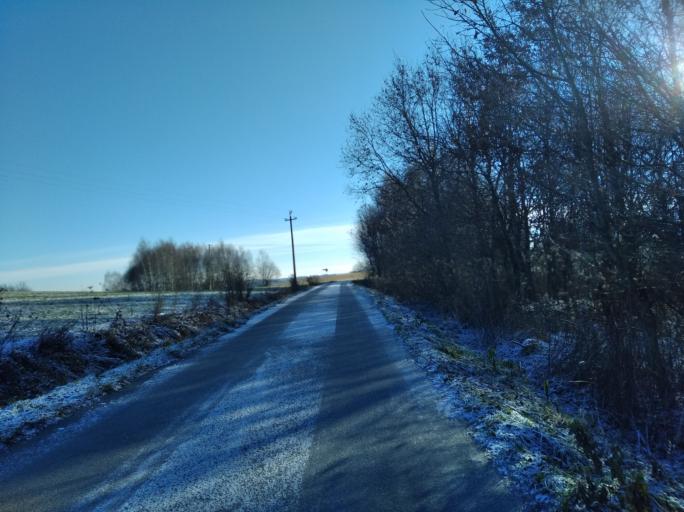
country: PL
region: Subcarpathian Voivodeship
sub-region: Powiat strzyzowski
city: Czudec
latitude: 49.9450
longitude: 21.7664
